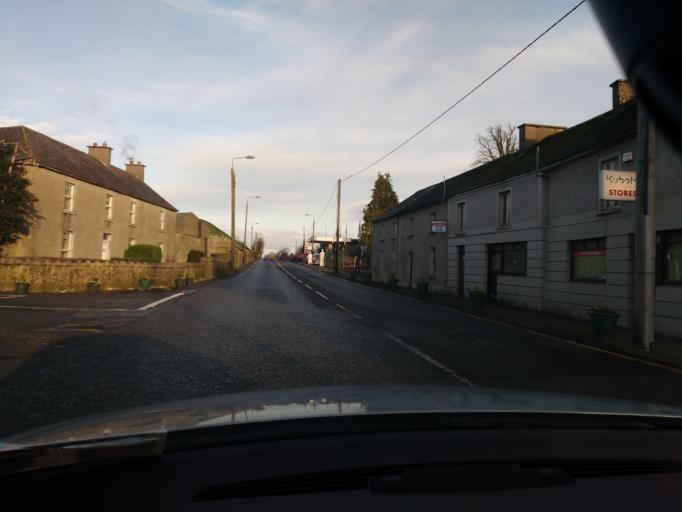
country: IE
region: Munster
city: Thurles
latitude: 52.6392
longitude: -7.7384
